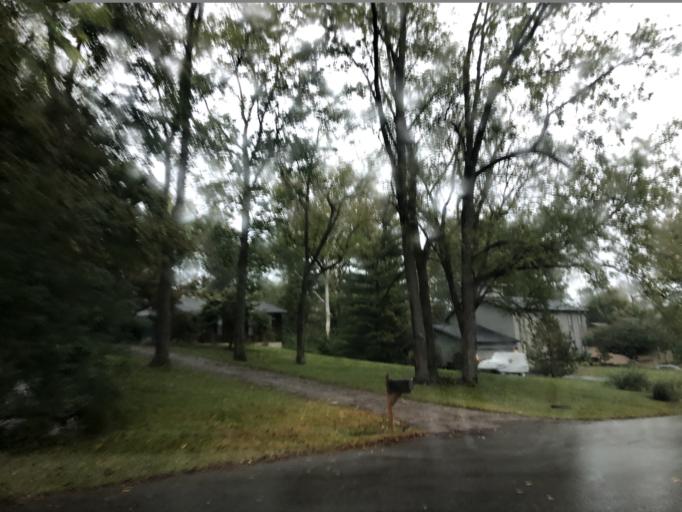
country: US
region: Ohio
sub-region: Hamilton County
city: Montgomery
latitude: 39.2299
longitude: -84.3238
